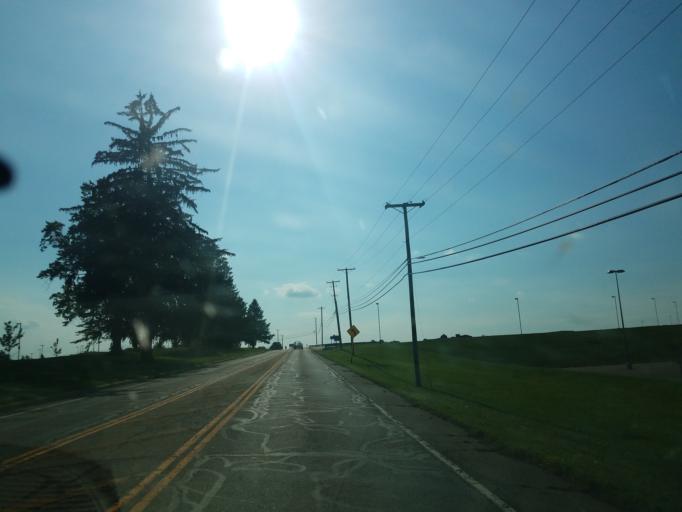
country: US
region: Ohio
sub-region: Stark County
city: Greentown
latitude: 40.9068
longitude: -81.4336
